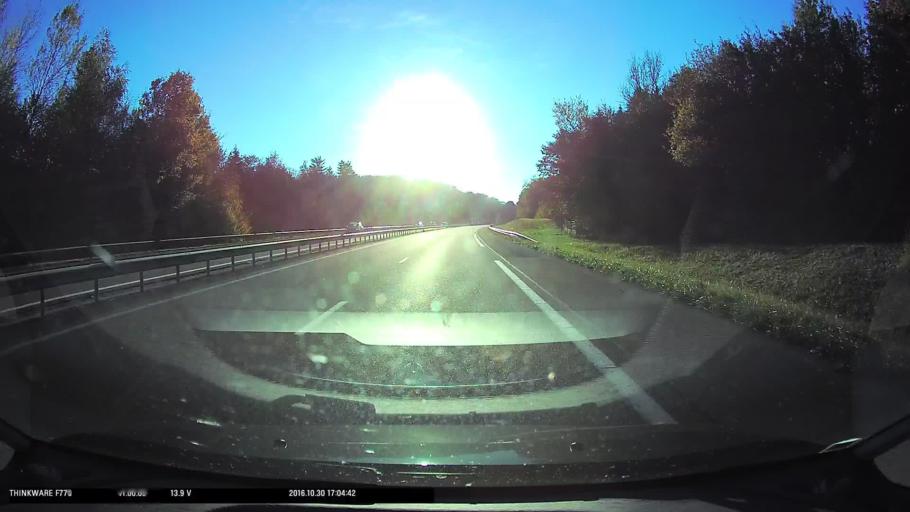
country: FR
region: Franche-Comte
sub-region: Departement du Jura
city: Orchamps
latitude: 47.1516
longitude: 5.6005
